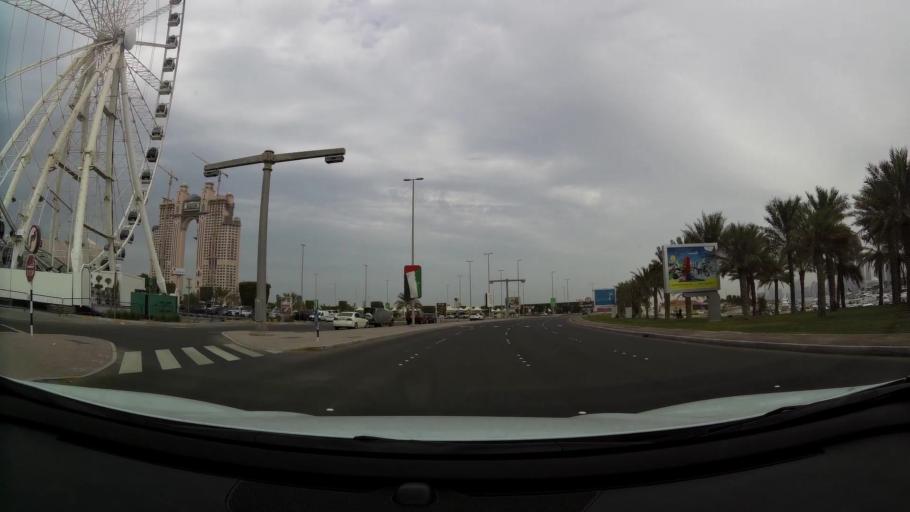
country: AE
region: Abu Dhabi
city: Abu Dhabi
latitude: 24.4750
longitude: 54.3236
